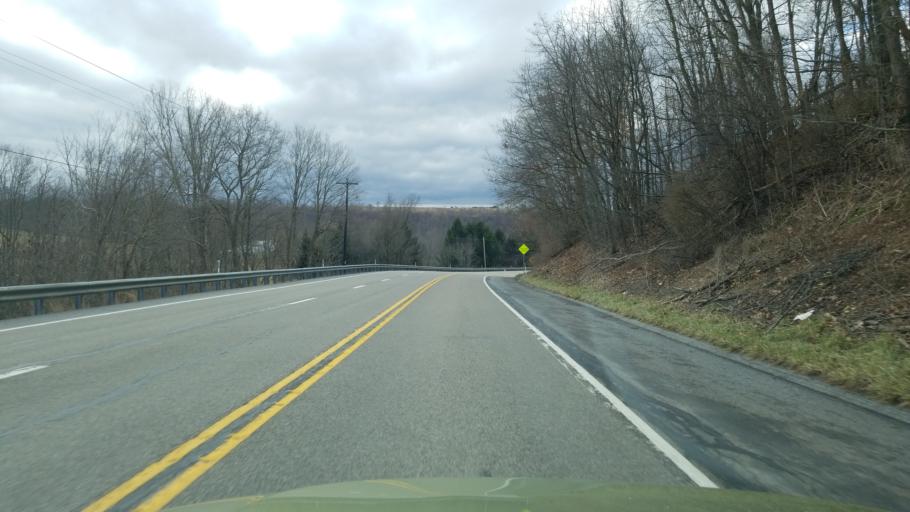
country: US
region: Pennsylvania
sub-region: Jefferson County
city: Punxsutawney
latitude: 40.8254
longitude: -79.0388
